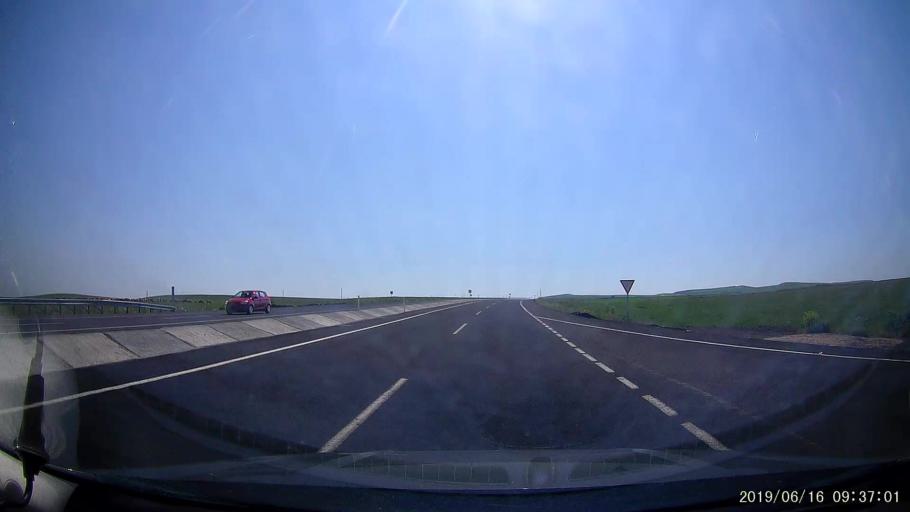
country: TR
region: Kars
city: Kars
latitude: 40.5552
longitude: 43.1854
